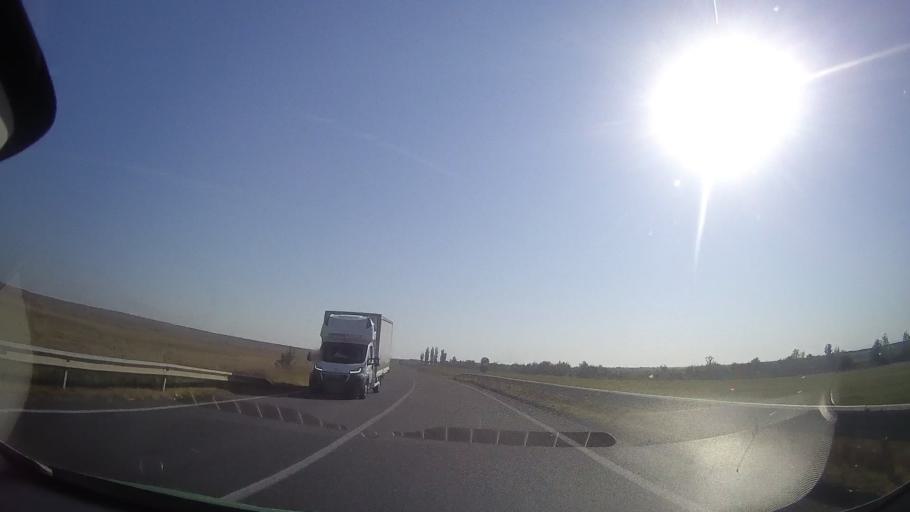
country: RO
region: Timis
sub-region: Comuna Topolovatu Mare
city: Topolovatu Mare
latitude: 45.7844
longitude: 21.5916
